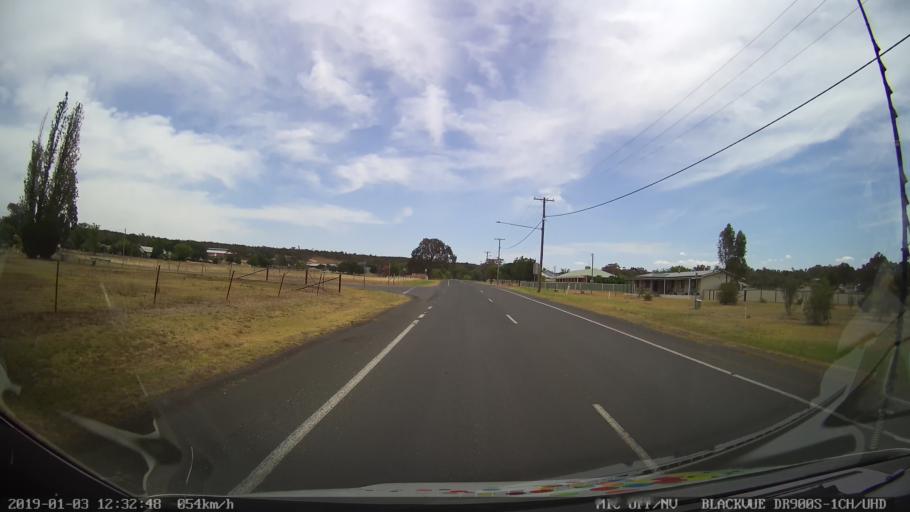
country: AU
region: New South Wales
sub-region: Weddin
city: Grenfell
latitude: -33.8905
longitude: 148.1620
